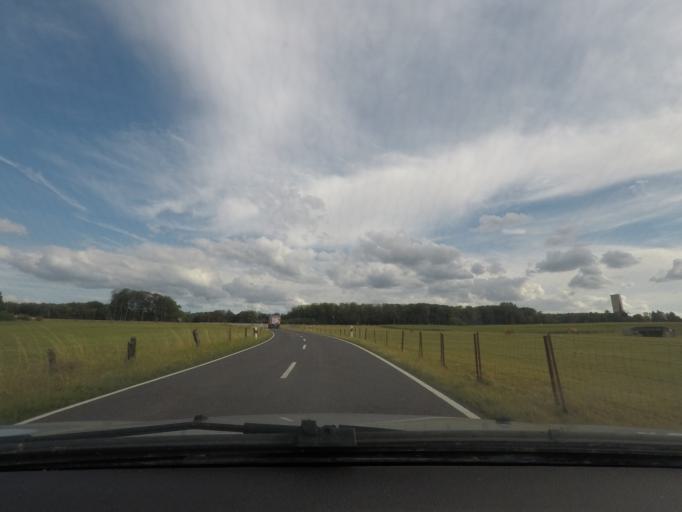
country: LU
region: Grevenmacher
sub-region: Canton d'Echternach
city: Consdorf
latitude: 49.7596
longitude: 6.3383
